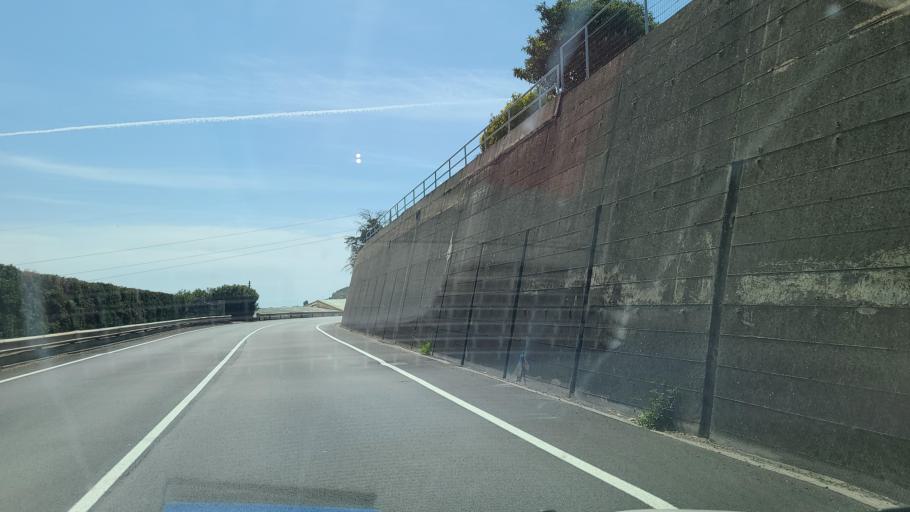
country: IT
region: Liguria
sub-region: Provincia di Imperia
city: Taggia
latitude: 43.8493
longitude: 7.8410
